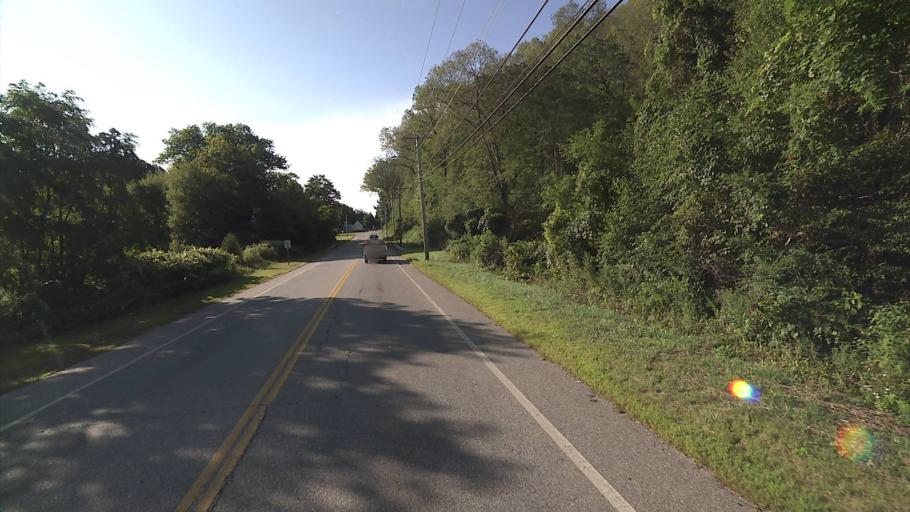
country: US
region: Connecticut
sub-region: New London County
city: Uncasville
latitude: 41.4483
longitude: -72.1055
